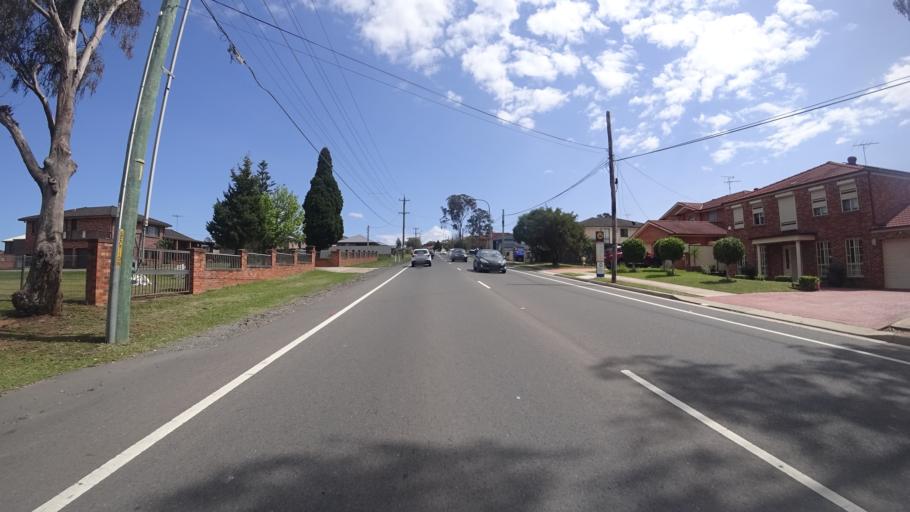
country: AU
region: New South Wales
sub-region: Campbelltown Municipality
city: Glenfield
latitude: -33.9615
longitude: 150.8967
